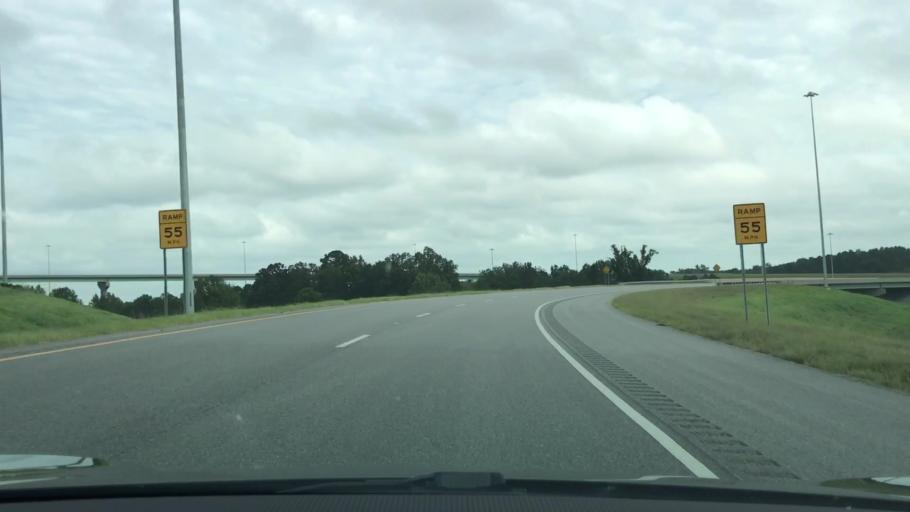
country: US
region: Alabama
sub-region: Montgomery County
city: Pike Road
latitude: 32.3646
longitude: -86.0777
